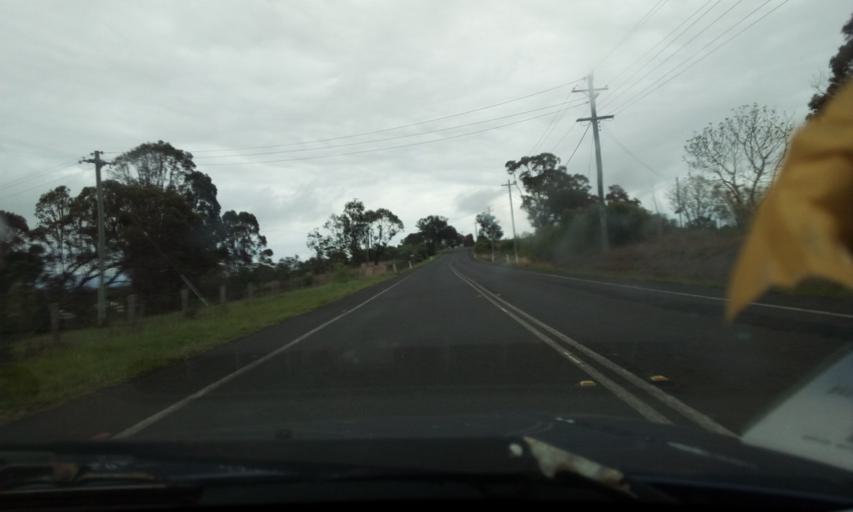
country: AU
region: New South Wales
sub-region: Wollondilly
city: Douglas Park
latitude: -34.1553
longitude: 150.7221
